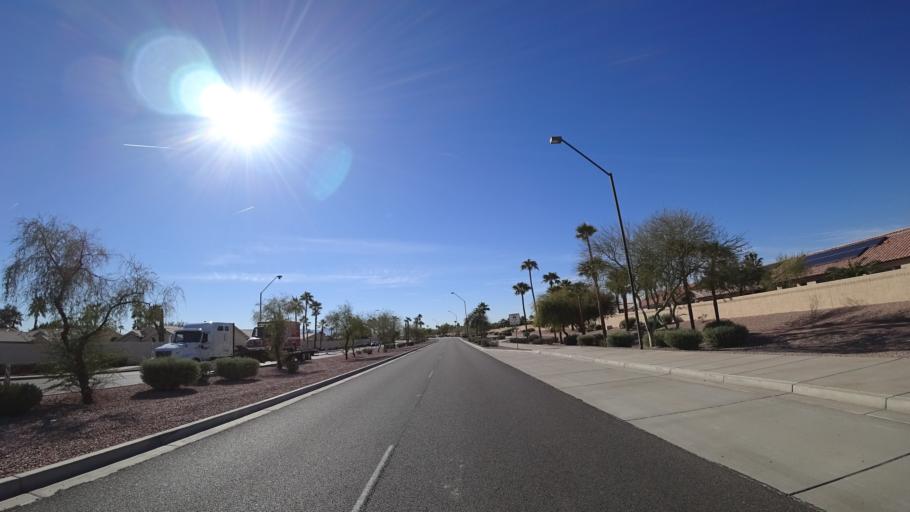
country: US
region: Arizona
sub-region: Maricopa County
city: Litchfield Park
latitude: 33.4933
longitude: -112.4013
